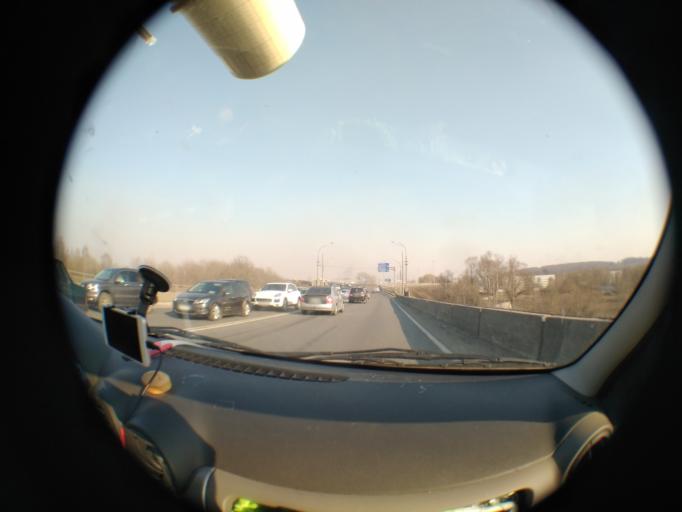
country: RU
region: Moskovskaya
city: Ostrovtsy
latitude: 55.5688
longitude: 38.0359
